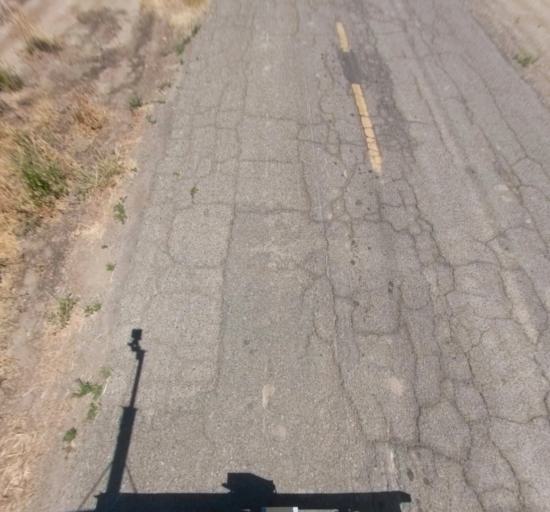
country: US
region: California
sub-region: Madera County
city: Chowchilla
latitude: 37.0584
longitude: -120.3469
